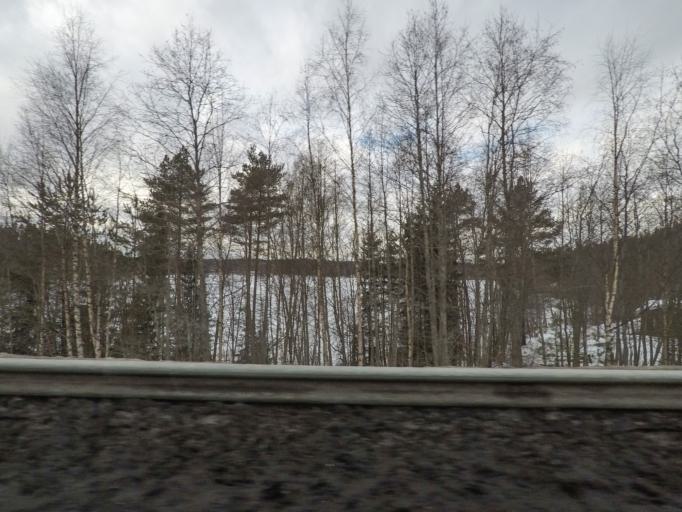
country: FI
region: Southern Savonia
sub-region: Mikkeli
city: Mikkeli
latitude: 61.6617
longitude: 27.2188
